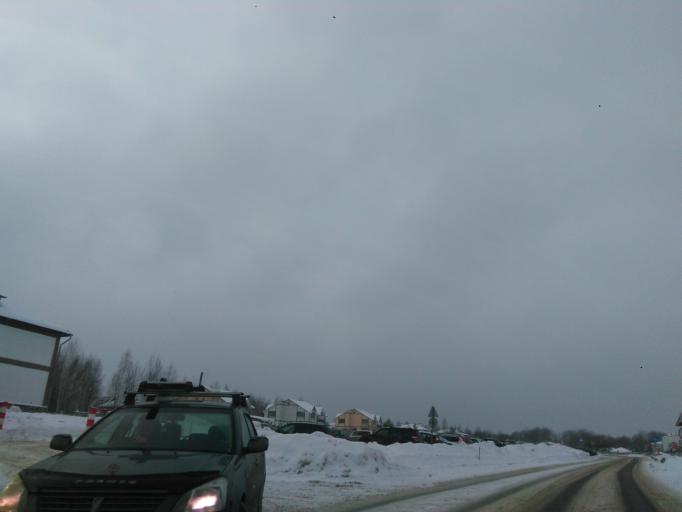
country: RU
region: Moskovskaya
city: Yakhroma
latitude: 56.2675
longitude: 37.4785
